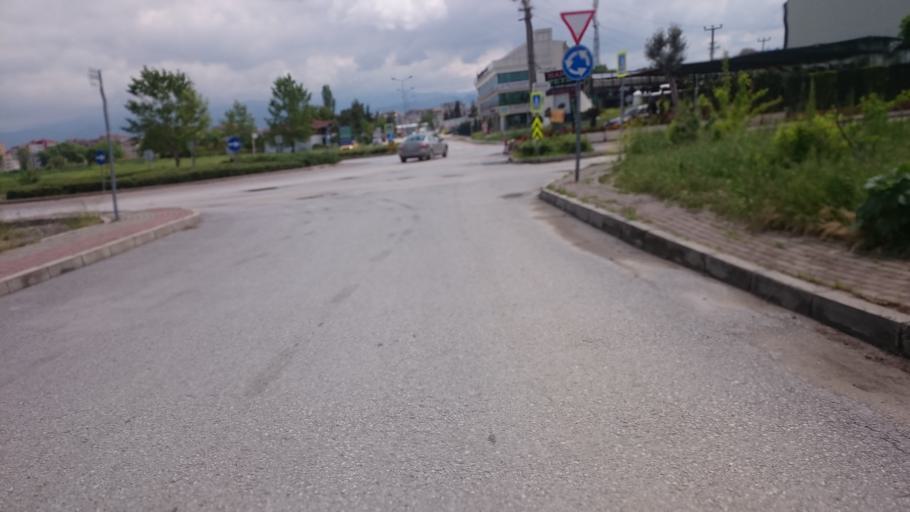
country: TR
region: Bursa
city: Niluefer
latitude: 40.2350
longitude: 28.9105
